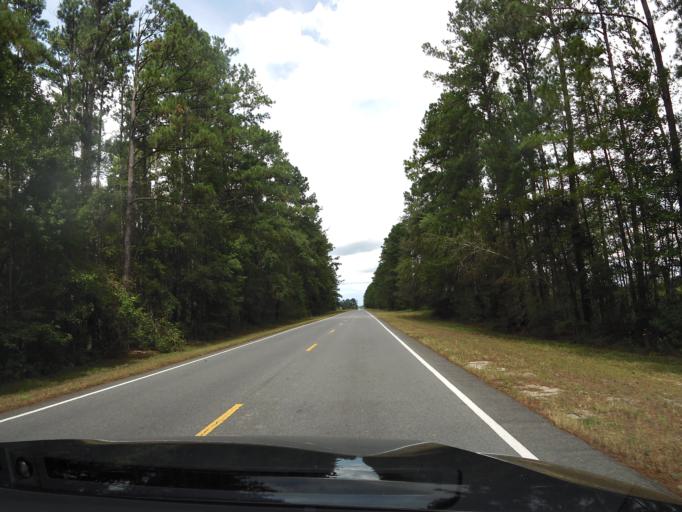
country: US
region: Georgia
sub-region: Brantley County
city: Nahunta
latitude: 31.0684
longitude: -82.0130
